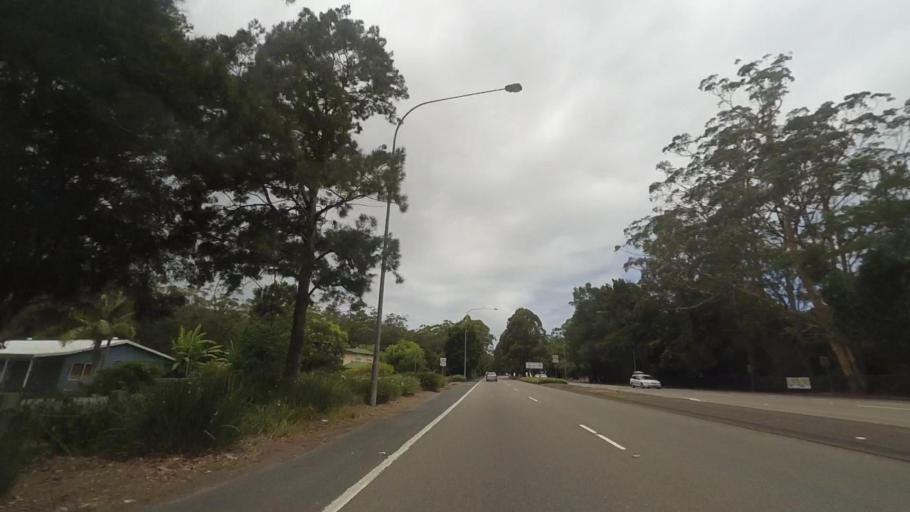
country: AU
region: New South Wales
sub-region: Wyong Shire
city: Berkeley Vale
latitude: -33.3424
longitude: 151.4289
